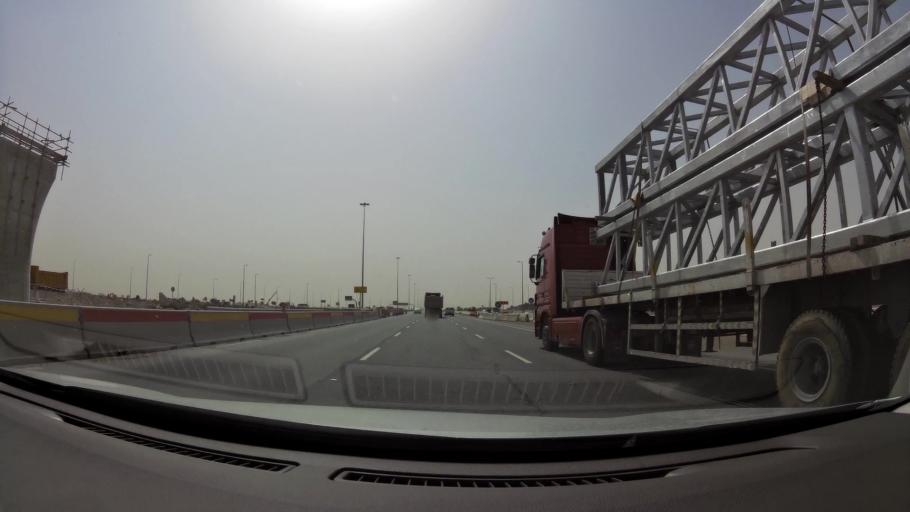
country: QA
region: Baladiyat ar Rayyan
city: Ar Rayyan
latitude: 25.1717
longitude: 51.3241
